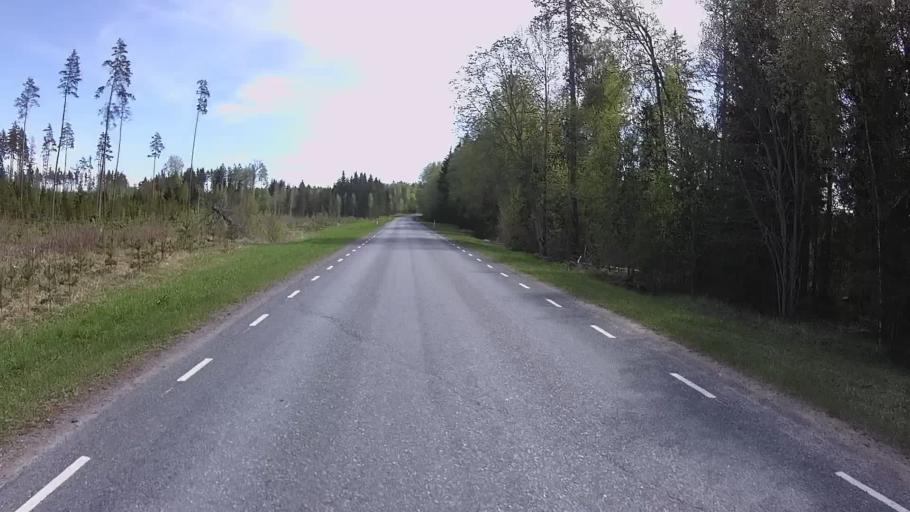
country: EE
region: Valgamaa
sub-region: Valga linn
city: Valga
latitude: 57.7063
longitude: 26.2374
